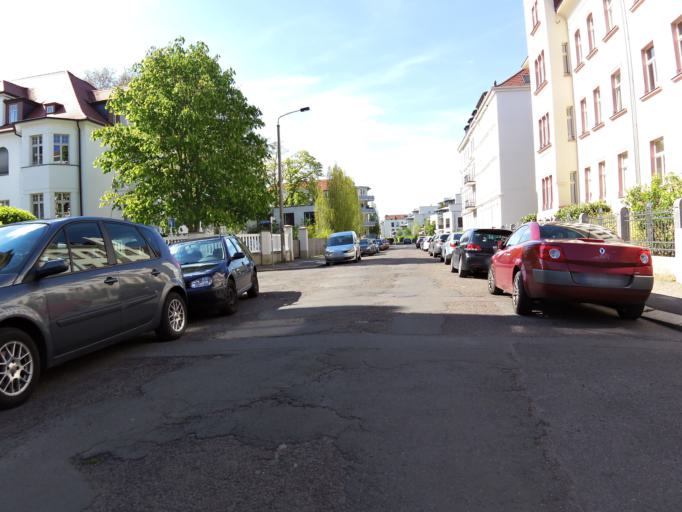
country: DE
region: Saxony
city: Leipzig
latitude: 51.3592
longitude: 12.3559
